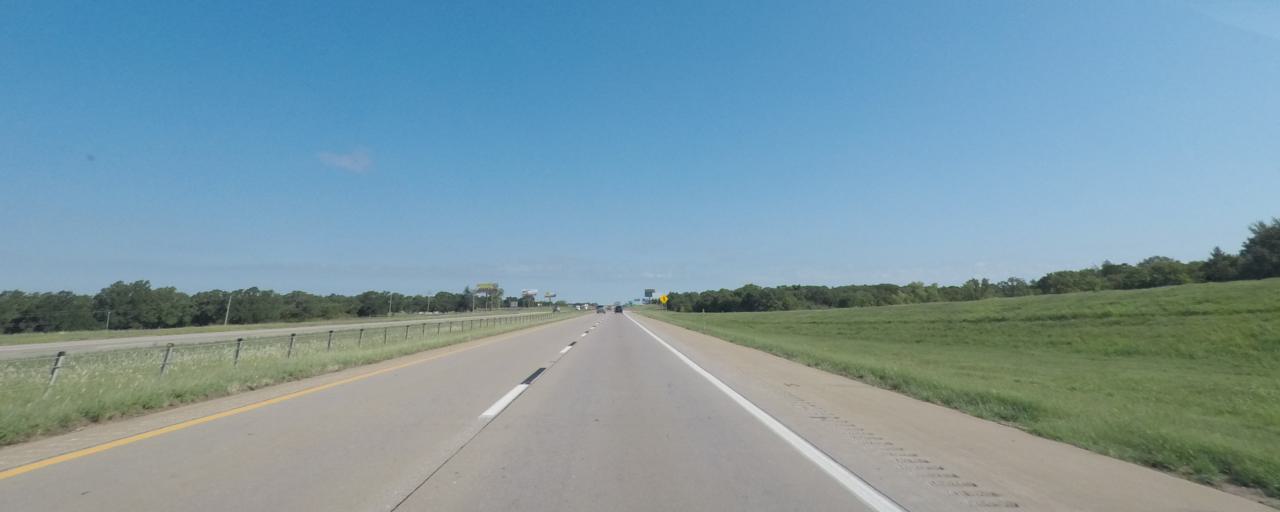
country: US
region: Oklahoma
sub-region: Logan County
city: Guthrie
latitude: 35.7990
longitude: -97.4162
